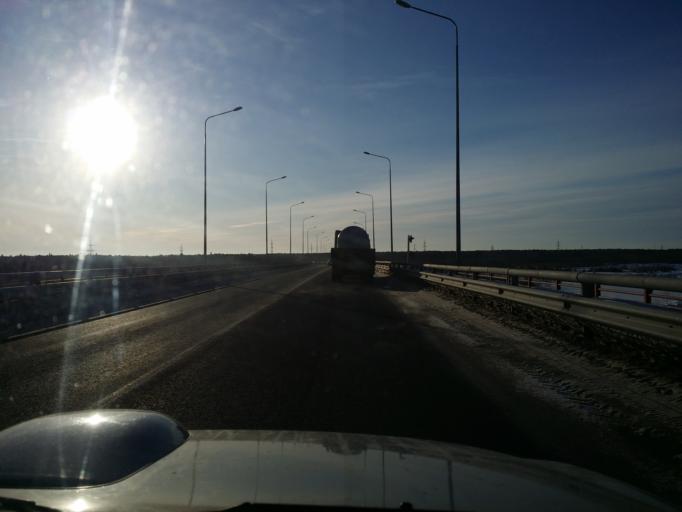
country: RU
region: Khanty-Mansiyskiy Avtonomnyy Okrug
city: Izluchinsk
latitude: 60.9353
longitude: 76.8882
